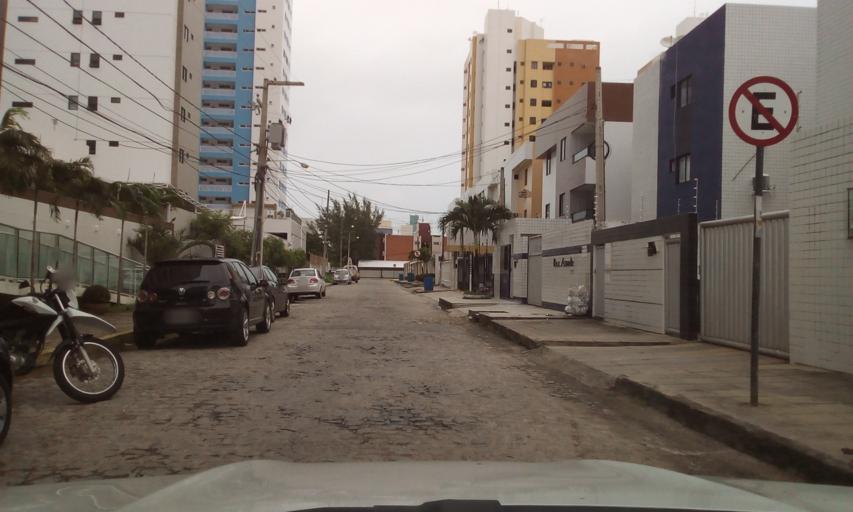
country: BR
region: Paraiba
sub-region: Joao Pessoa
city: Joao Pessoa
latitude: -7.0825
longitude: -34.8389
